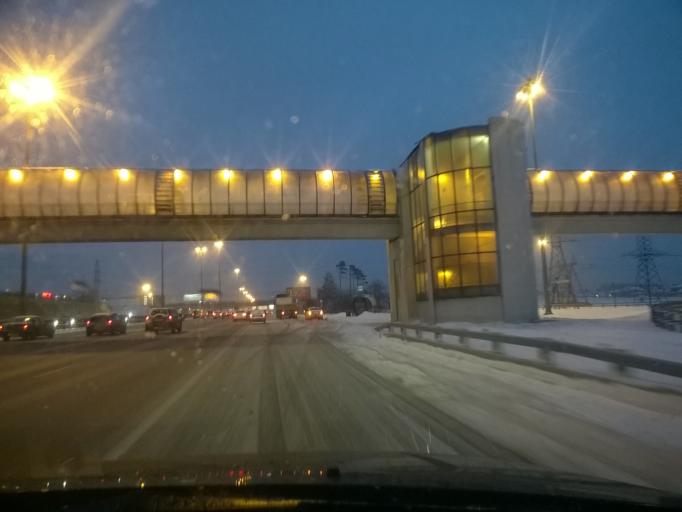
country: RU
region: Moskovskaya
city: Mosrentgen
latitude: 55.6295
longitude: 37.4327
